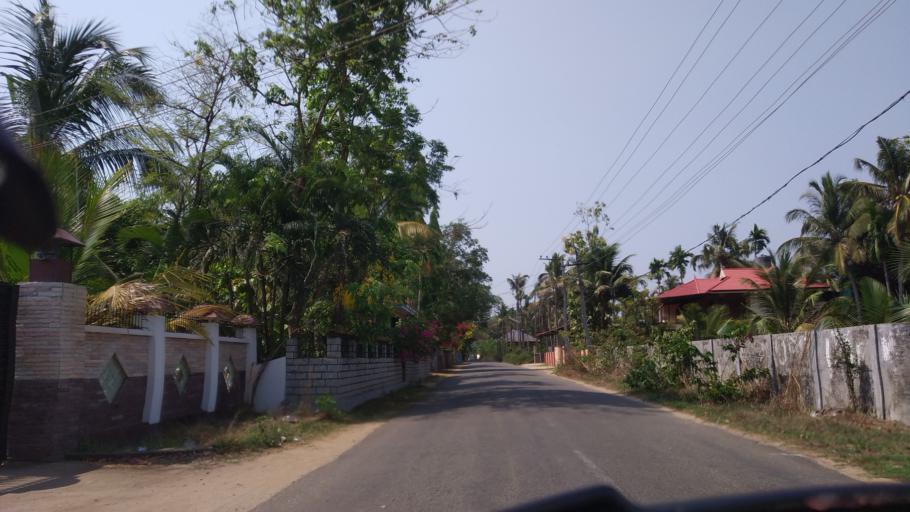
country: IN
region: Kerala
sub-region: Thrissur District
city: Kodungallur
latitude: 10.2585
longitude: 76.1455
